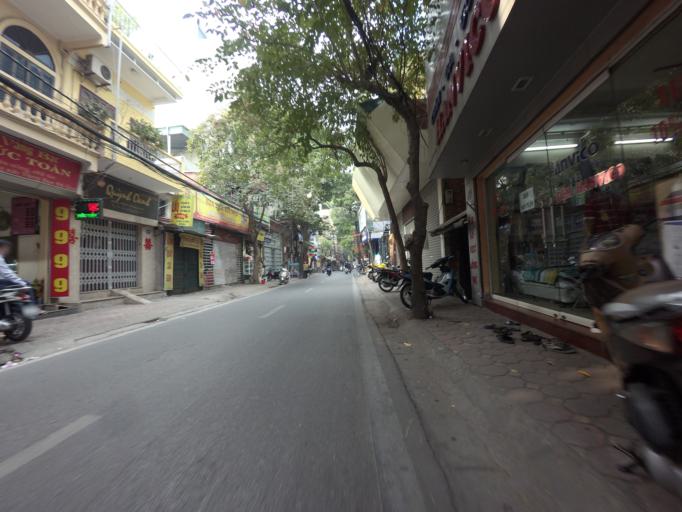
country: VN
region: Ha Noi
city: Hoan Kiem
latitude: 21.0534
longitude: 105.8362
